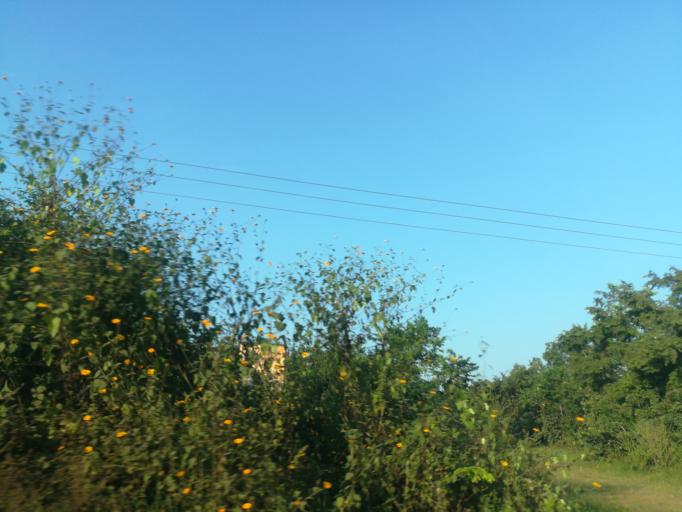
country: NG
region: Ogun
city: Abeokuta
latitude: 7.2125
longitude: 3.1964
